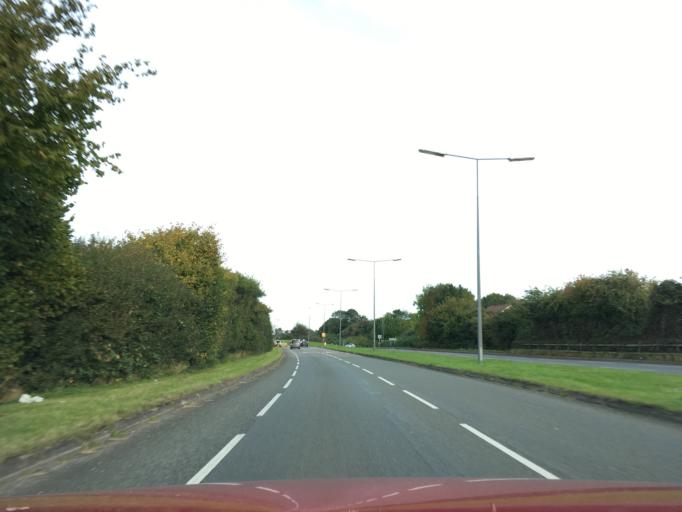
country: GB
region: England
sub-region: South Gloucestershire
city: Stoke Gifford
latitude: 51.5217
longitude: -2.5340
